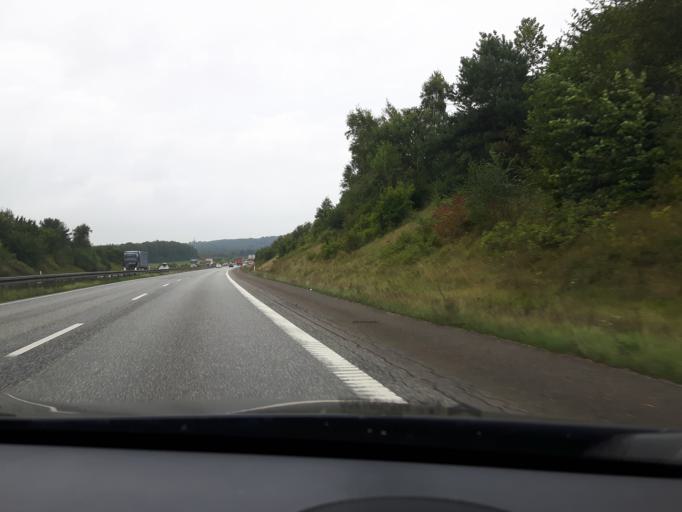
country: DK
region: North Denmark
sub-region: Mariagerfjord Kommune
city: Hobro
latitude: 56.6063
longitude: 9.7449
